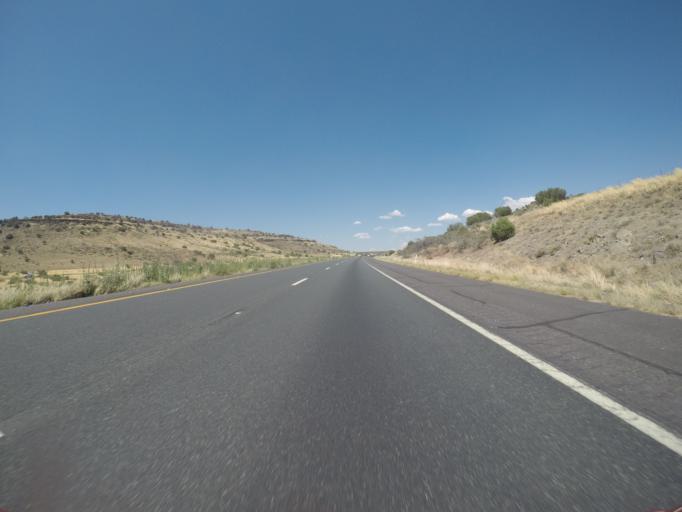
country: US
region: Arizona
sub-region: Yavapai County
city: Camp Verde
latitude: 34.4803
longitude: -112.0183
